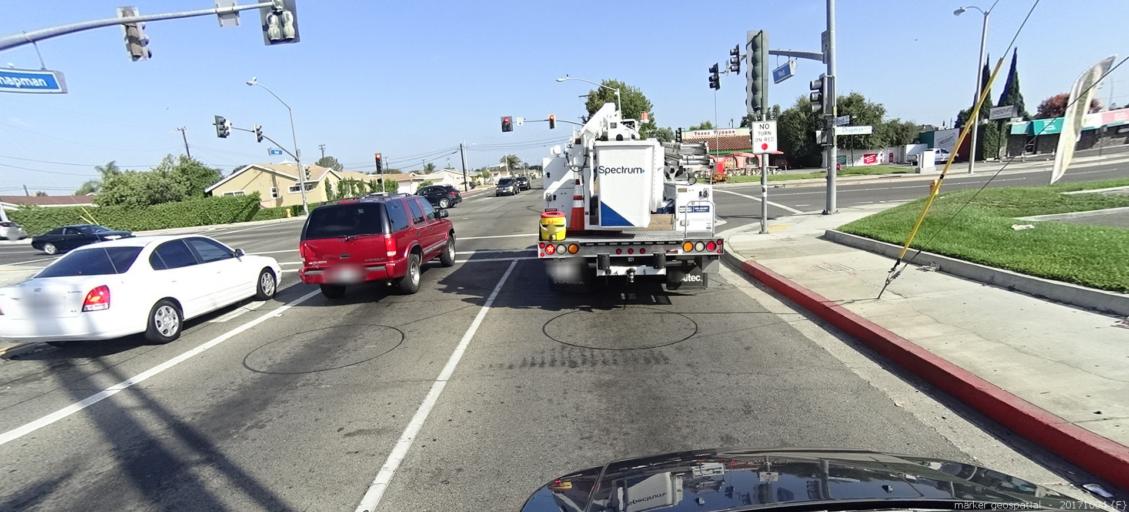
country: US
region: California
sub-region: Orange County
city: Garden Grove
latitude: 33.7885
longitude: -117.9237
